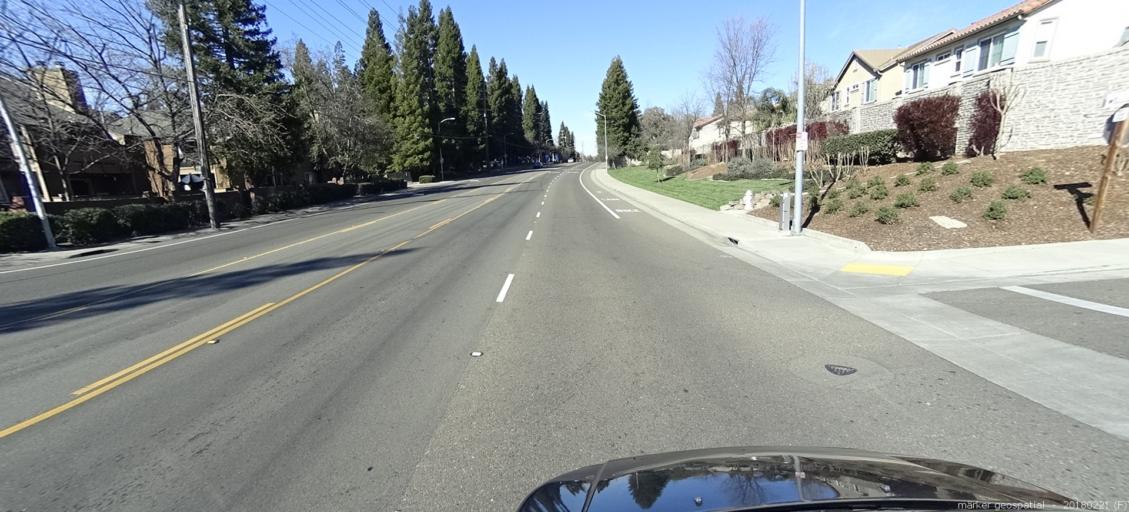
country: US
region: California
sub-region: Sacramento County
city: Citrus Heights
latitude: 38.6819
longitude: -121.2624
